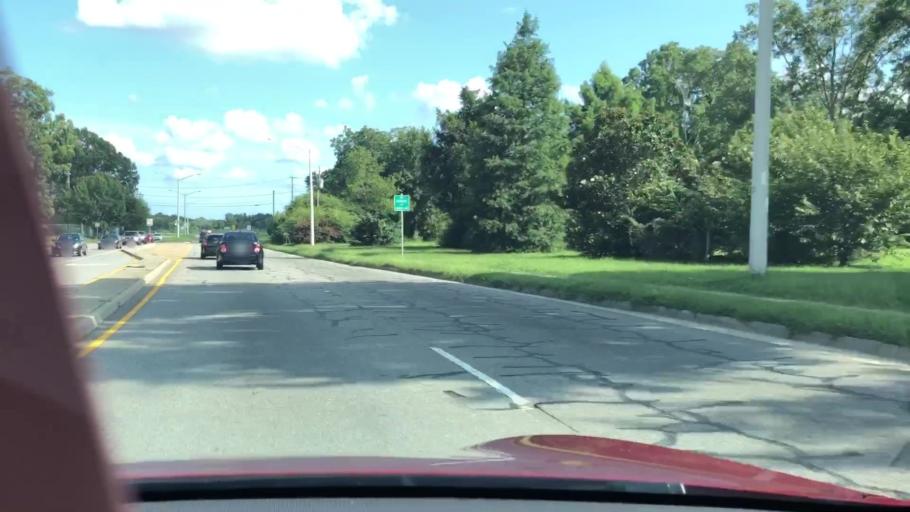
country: US
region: Virginia
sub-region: City of Virginia Beach
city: Virginia Beach
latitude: 36.8399
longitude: -76.0208
